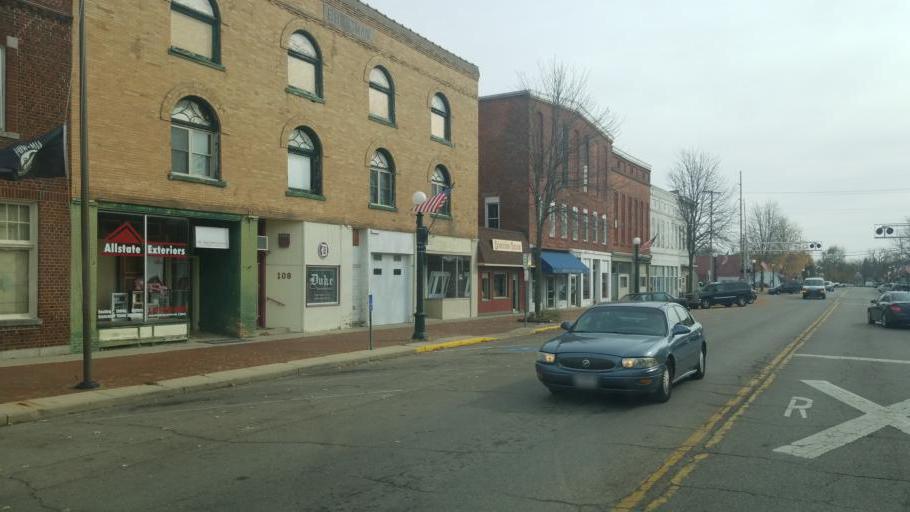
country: US
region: Ohio
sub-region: Madison County
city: London
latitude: 39.8848
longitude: -83.4468
